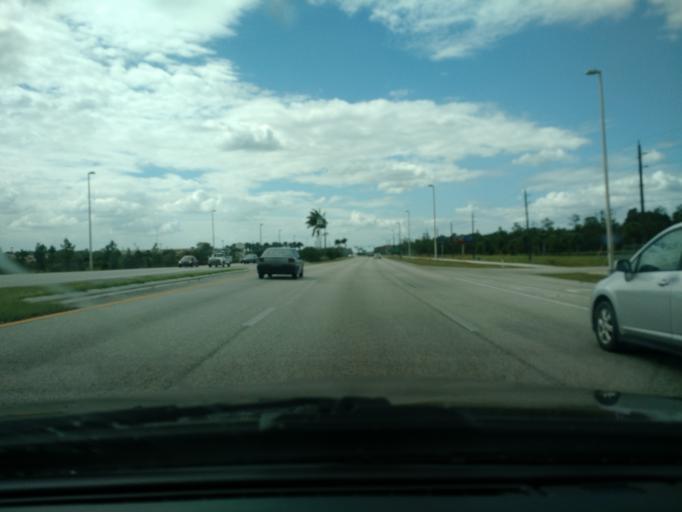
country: US
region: Florida
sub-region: Lee County
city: Gateway
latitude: 26.6130
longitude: -81.7775
